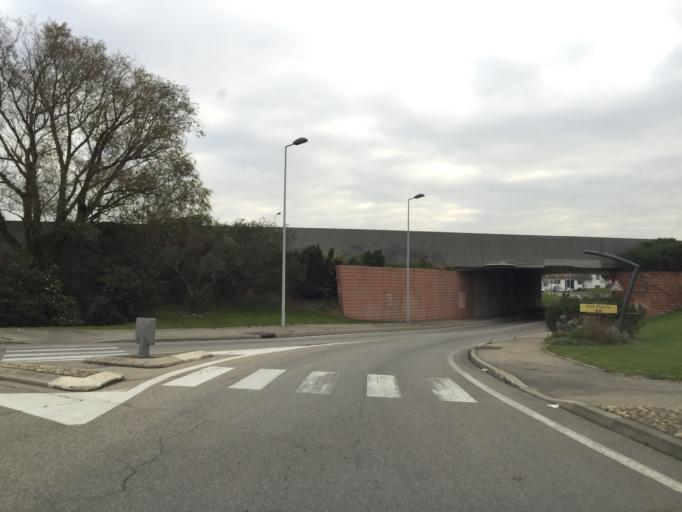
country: FR
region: Provence-Alpes-Cote d'Azur
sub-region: Departement du Vaucluse
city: Sorgues
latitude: 44.0181
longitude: 4.8687
